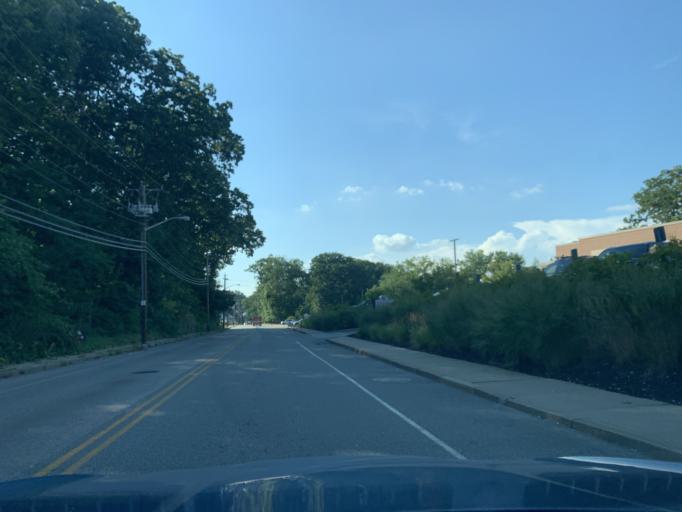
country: US
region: Rhode Island
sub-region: Kent County
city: West Warwick
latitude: 41.7050
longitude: -71.4789
